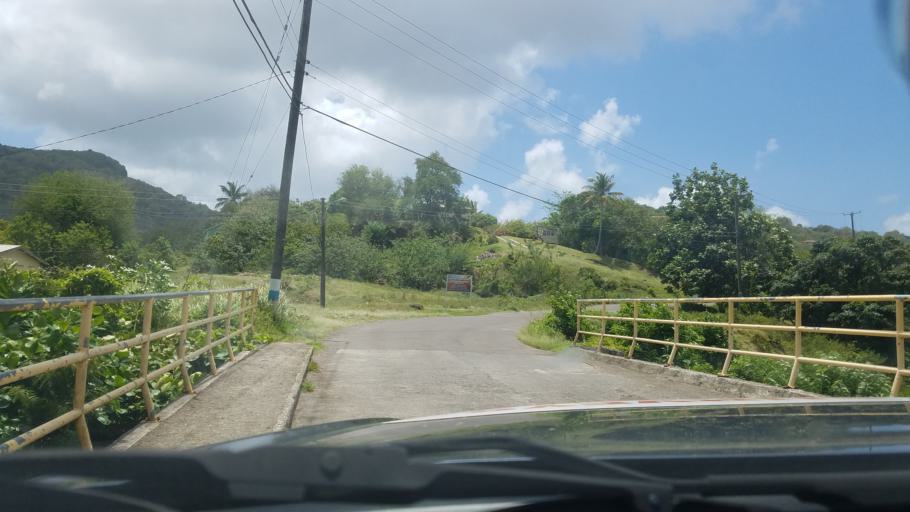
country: LC
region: Gros-Islet
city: Gros Islet
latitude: 14.0535
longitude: -60.9311
